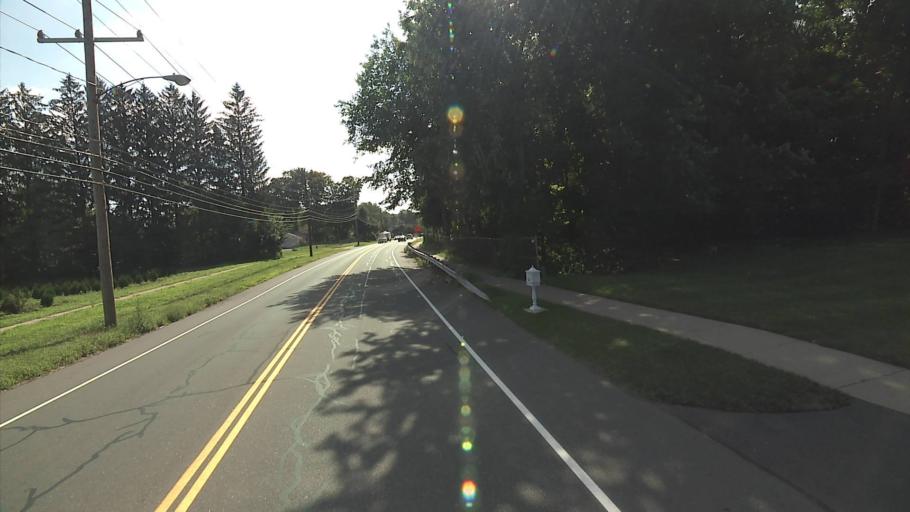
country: US
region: Connecticut
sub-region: Hartford County
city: Hazardville
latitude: 41.9860
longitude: -72.5271
